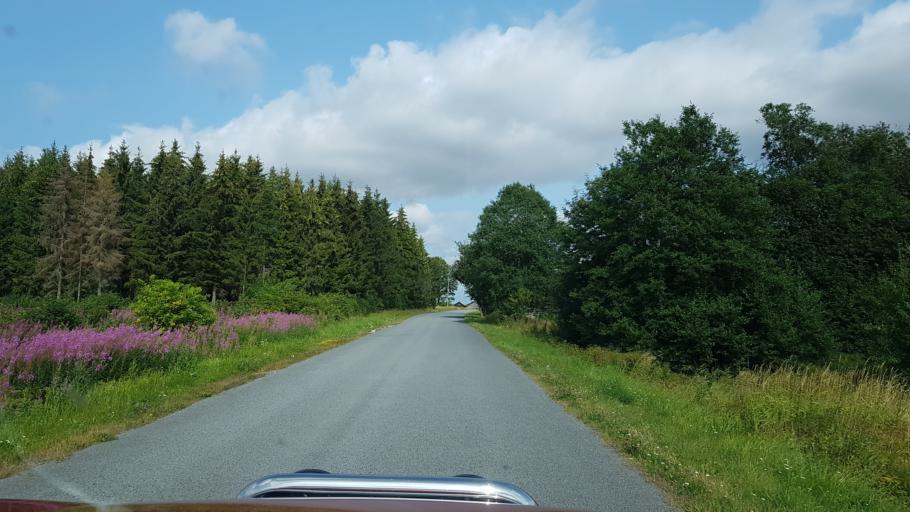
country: EE
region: Laeaene-Virumaa
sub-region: Kadrina vald
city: Kadrina
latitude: 59.3365
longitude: 26.0496
